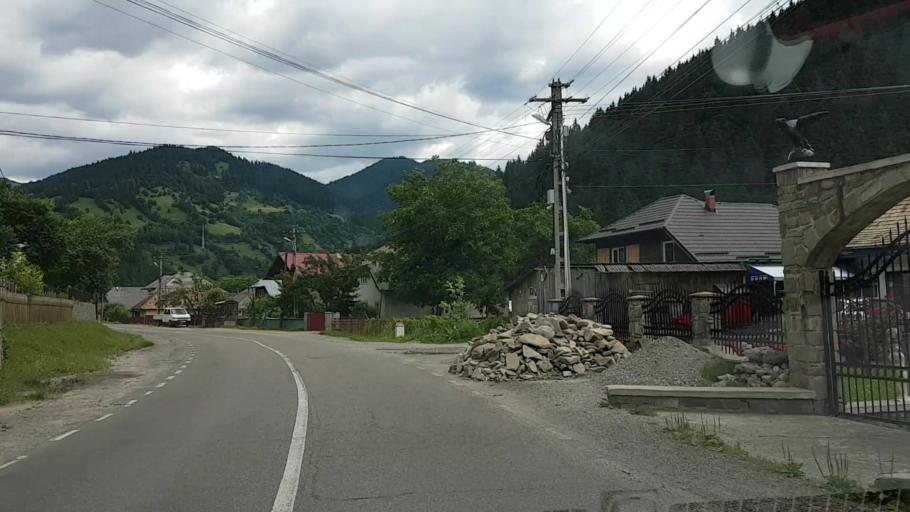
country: RO
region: Neamt
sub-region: Comuna Borca
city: Borca
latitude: 47.2165
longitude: 25.7428
